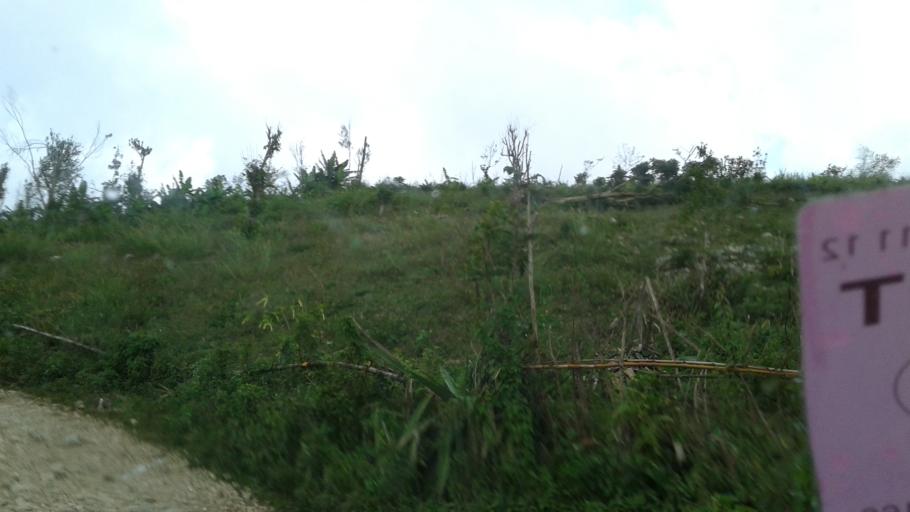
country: HT
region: Grandans
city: Jeremie
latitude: 18.4939
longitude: -74.1100
